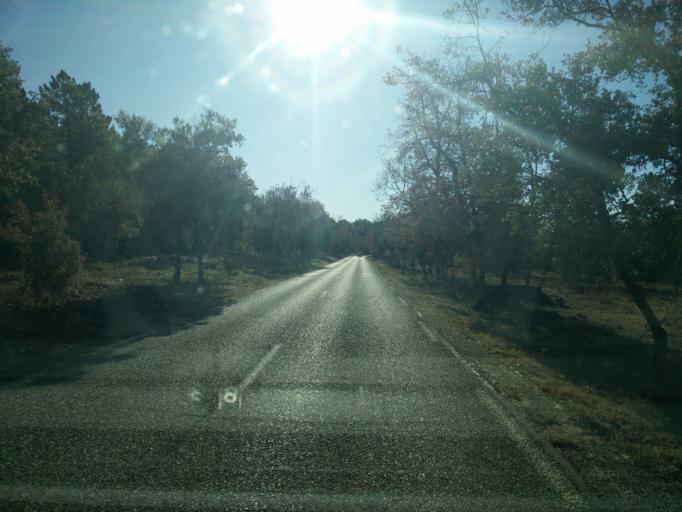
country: FR
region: Provence-Alpes-Cote d'Azur
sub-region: Departement du Var
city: Aups
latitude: 43.6061
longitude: 6.2193
